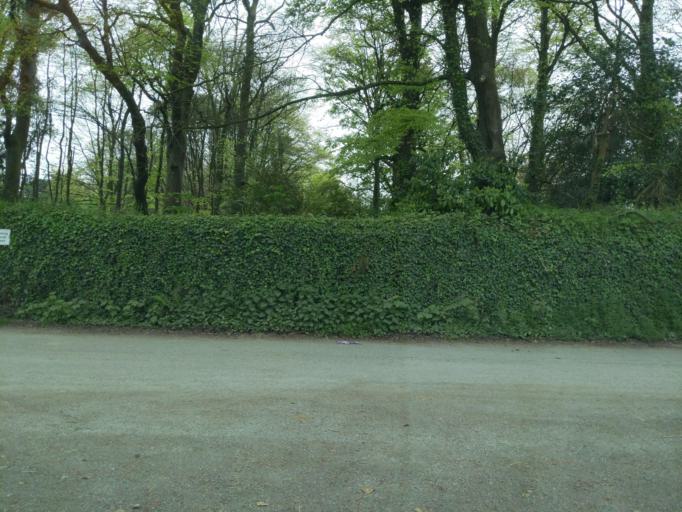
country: GB
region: England
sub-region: Cornwall
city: St Austell
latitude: 50.3080
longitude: -4.7642
